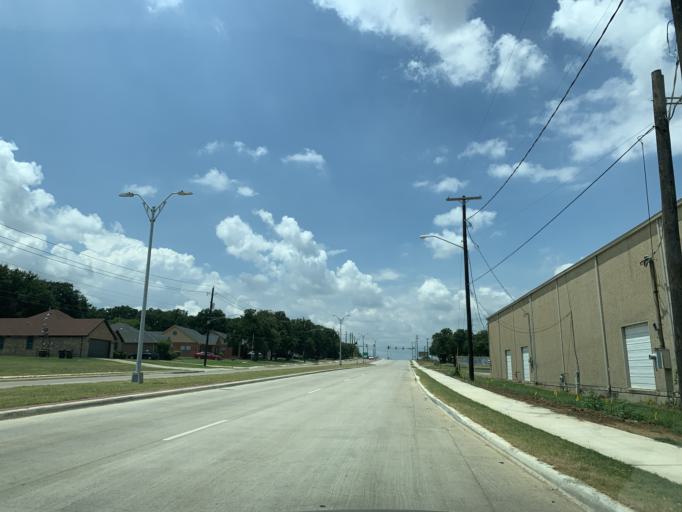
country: US
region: Texas
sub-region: Tarrant County
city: Forest Hill
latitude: 32.7301
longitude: -97.2345
